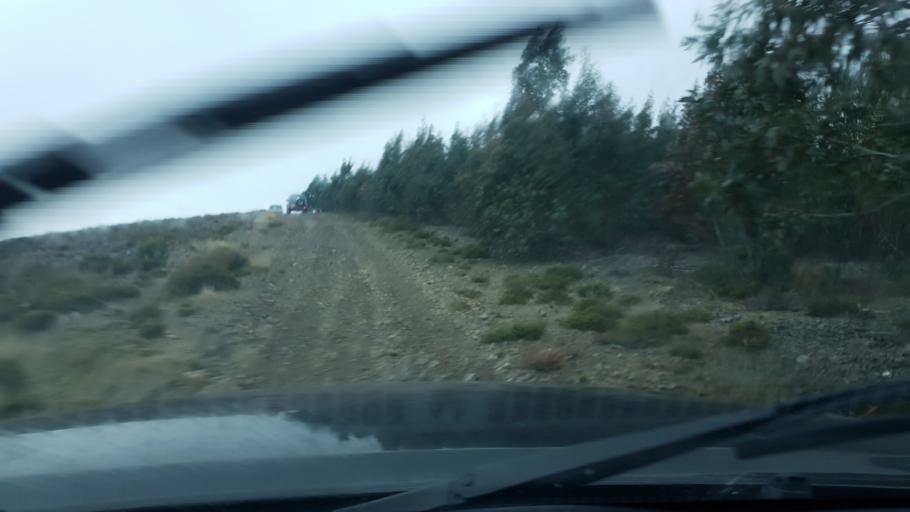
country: PT
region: Viseu
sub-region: Sao Pedro do Sul
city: Sao Pedro do Sul
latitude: 40.8646
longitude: -8.0922
